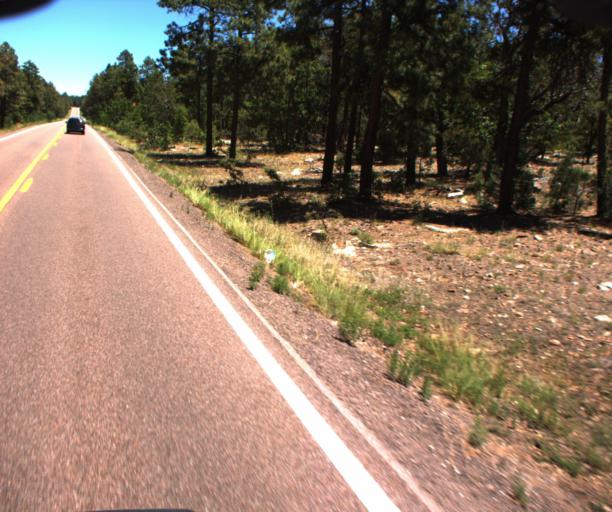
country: US
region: Arizona
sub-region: Gila County
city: Pine
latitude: 34.4348
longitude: -111.5032
